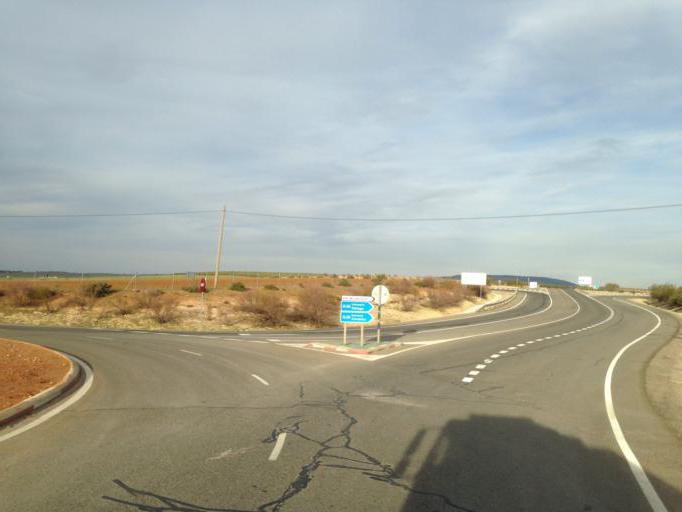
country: ES
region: Andalusia
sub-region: Provincia de Malaga
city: Mollina
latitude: 37.1108
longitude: -4.5670
